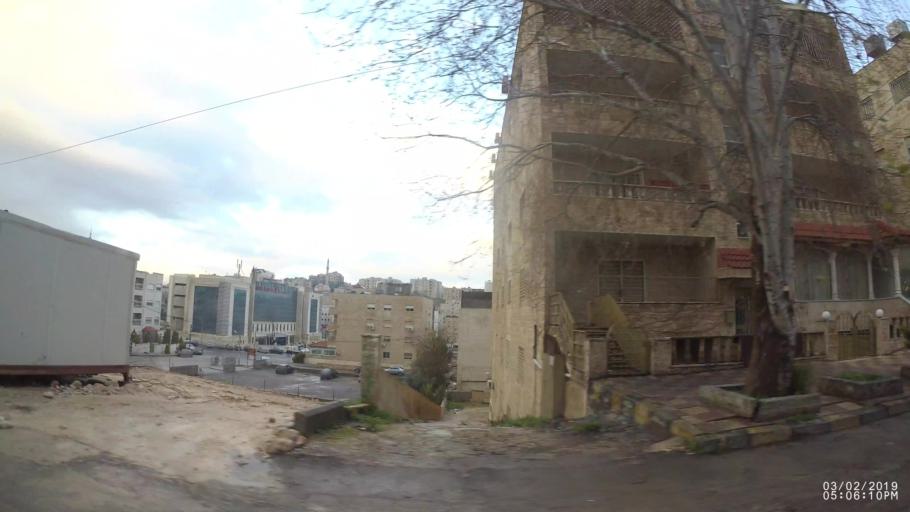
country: JO
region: Amman
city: Amman
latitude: 31.9879
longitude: 35.9157
